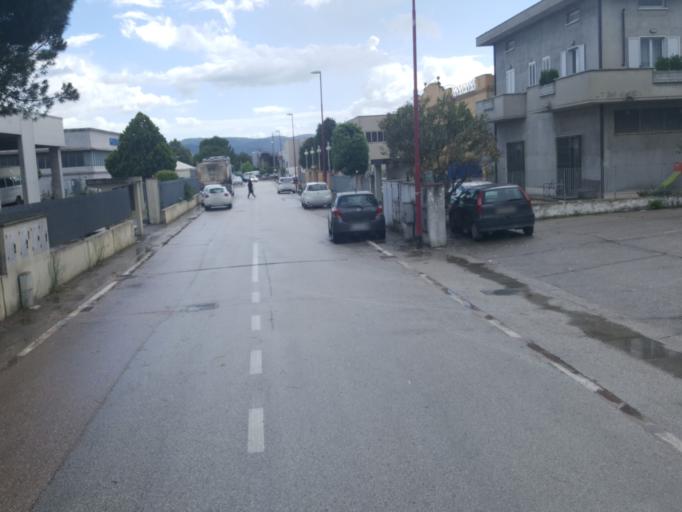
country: IT
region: Umbria
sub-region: Provincia di Perugia
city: Bastia umbra
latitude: 43.0541
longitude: 12.5483
